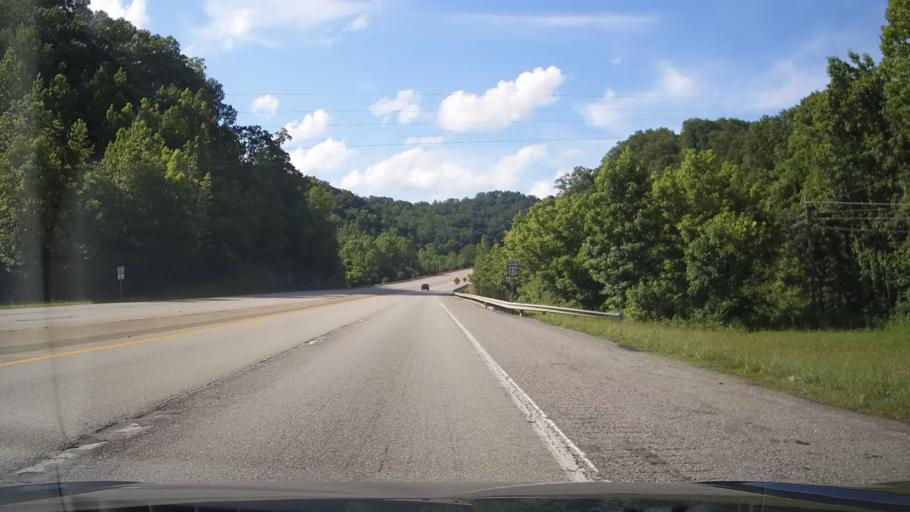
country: US
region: Kentucky
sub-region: Lawrence County
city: Louisa
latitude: 38.0241
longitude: -82.6517
